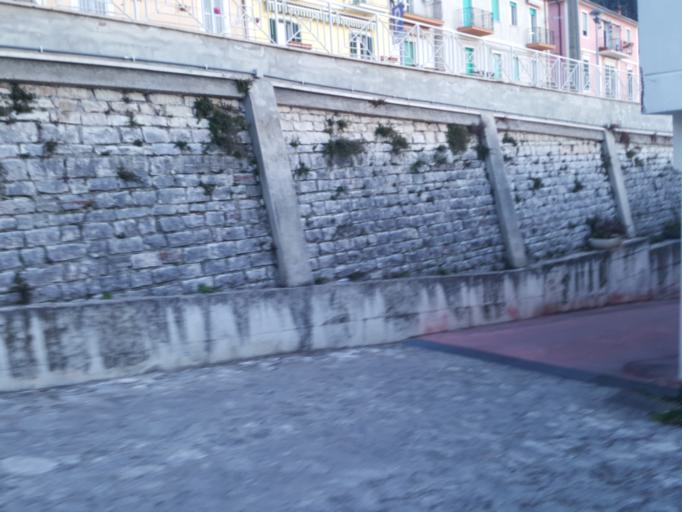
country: IT
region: Latium
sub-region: Provincia di Rieti
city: Labro
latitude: 42.5349
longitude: 12.7603
